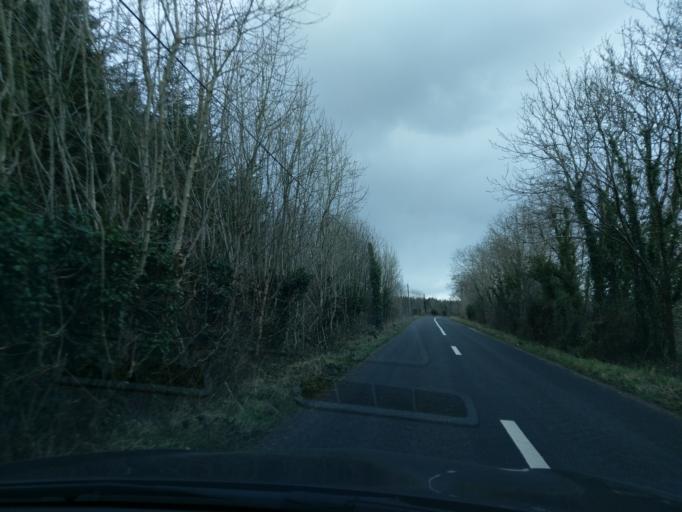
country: IE
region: Connaught
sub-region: County Galway
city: Athenry
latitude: 53.3992
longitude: -8.6274
